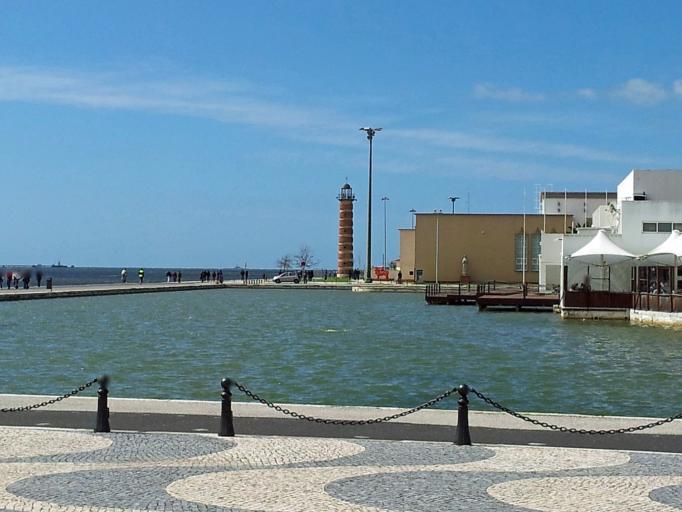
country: PT
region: Lisbon
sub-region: Oeiras
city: Alges
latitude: 38.6938
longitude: -9.2061
